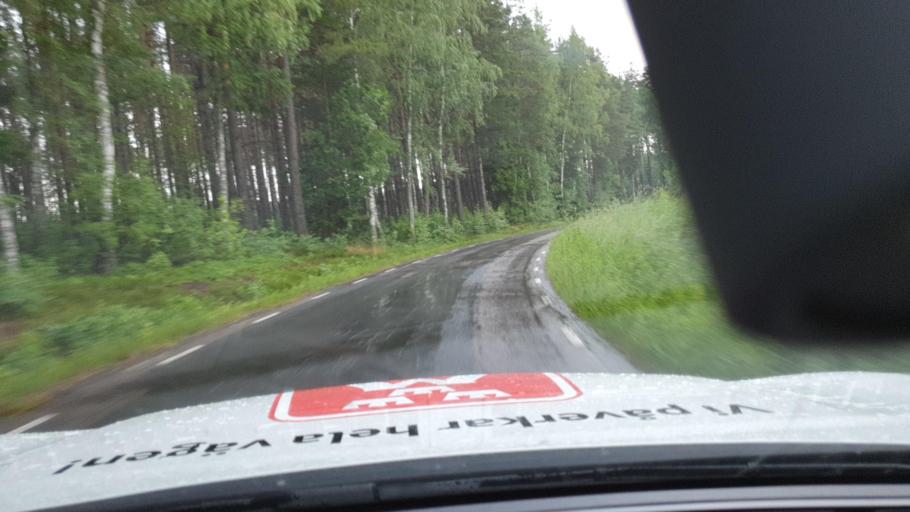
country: SE
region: Vaestra Goetaland
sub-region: Skovde Kommun
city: Stopen
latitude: 58.4665
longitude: 13.9178
